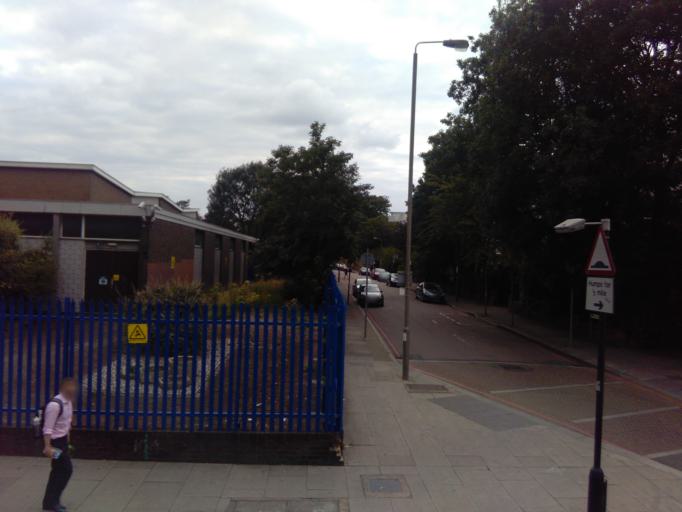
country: GB
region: England
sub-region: Greater London
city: Earlsfield
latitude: 51.4375
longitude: -0.1573
